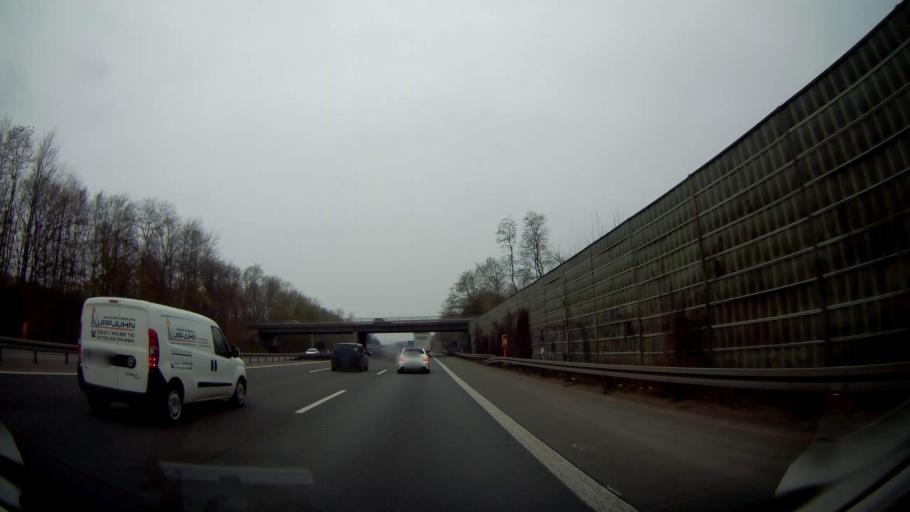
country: DE
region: North Rhine-Westphalia
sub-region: Regierungsbezirk Munster
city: Recklinghausen
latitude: 51.5925
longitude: 7.2360
